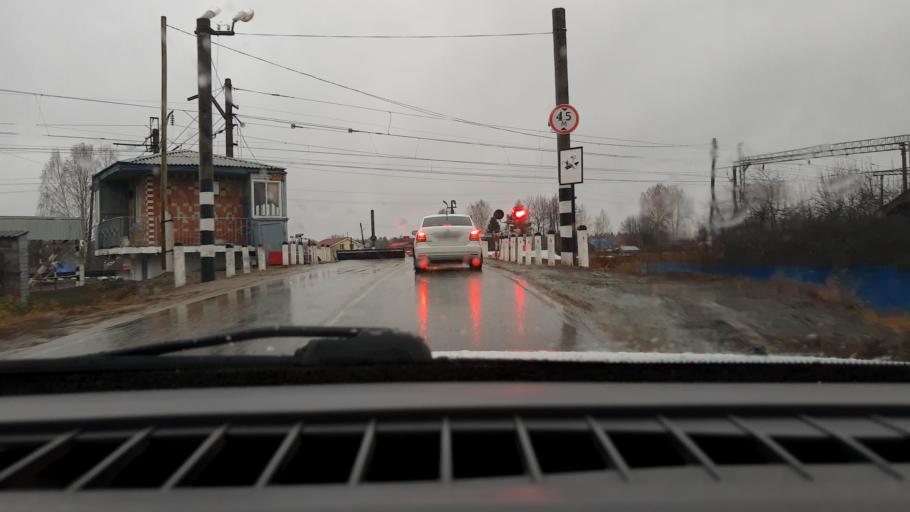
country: RU
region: Nizjnij Novgorod
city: Linda
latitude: 56.6857
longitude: 44.2023
